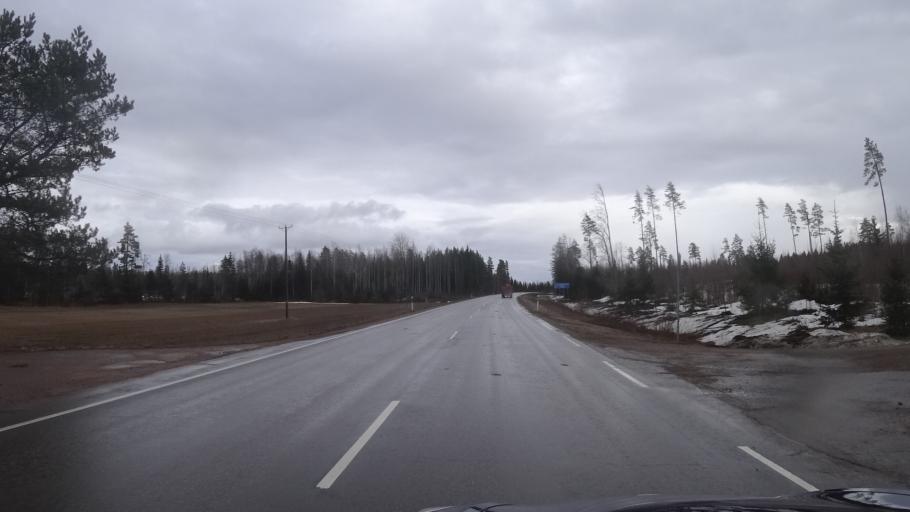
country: FI
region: Kymenlaakso
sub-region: Kouvola
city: Elimaeki
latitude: 60.7125
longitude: 26.4677
